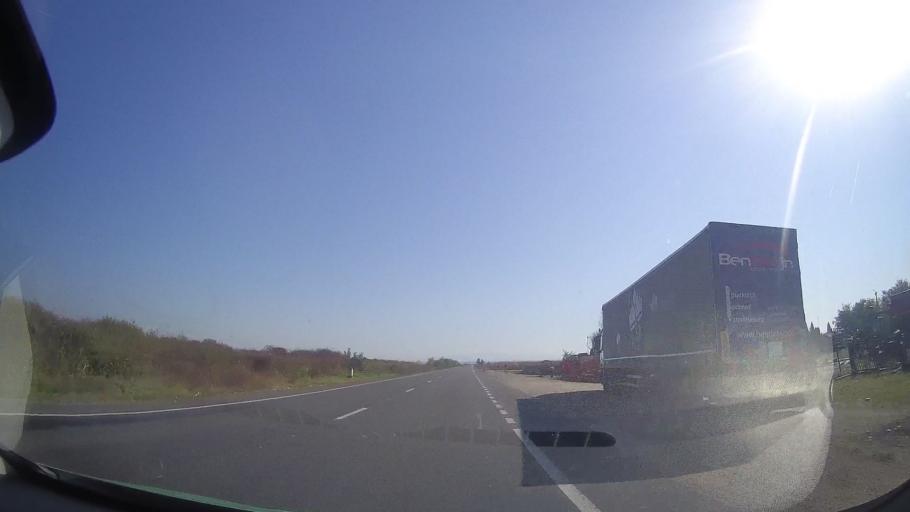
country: RO
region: Timis
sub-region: Comuna Belint
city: Belint
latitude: 45.7478
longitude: 21.7831
